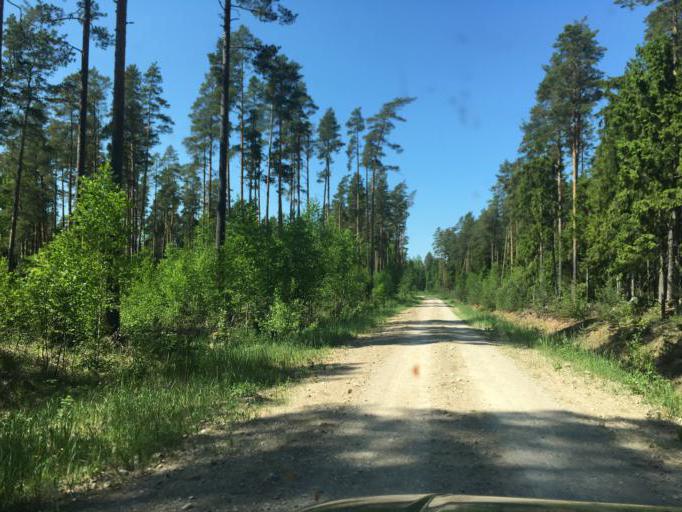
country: LV
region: Talsu Rajons
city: Valdemarpils
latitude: 57.4437
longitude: 22.6627
